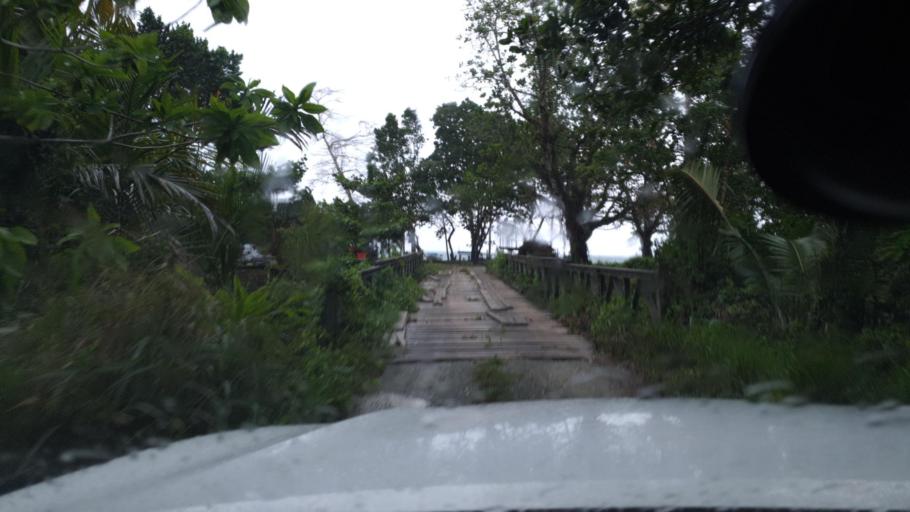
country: SB
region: Central Province
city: Tulaghi
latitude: -9.4470
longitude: 160.3949
